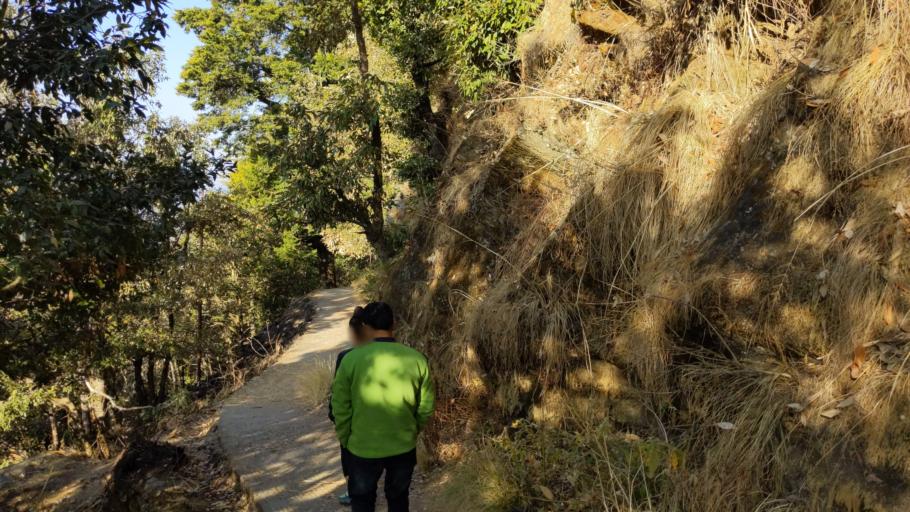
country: IN
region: Uttarakhand
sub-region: Almora
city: Almora
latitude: 29.4743
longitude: 79.6454
